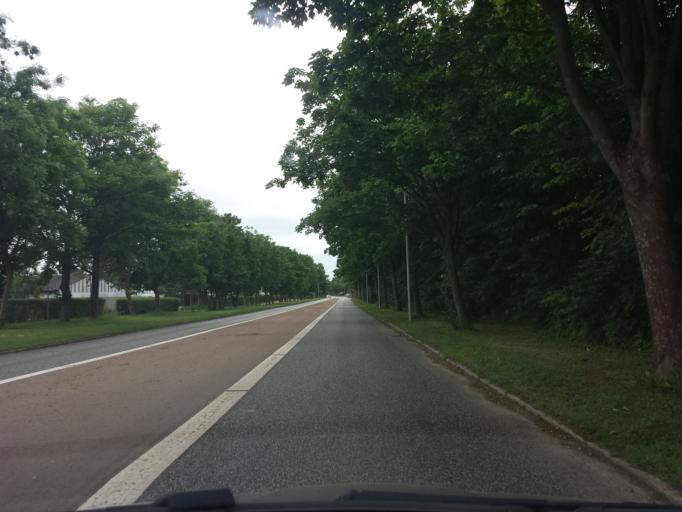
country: DK
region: Capital Region
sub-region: Albertslund Kommune
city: Albertslund
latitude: 55.6730
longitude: 12.3711
